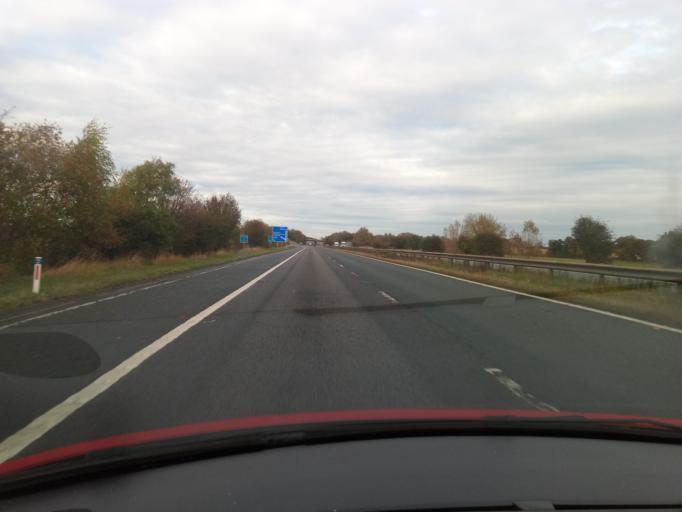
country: GB
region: England
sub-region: Darlington
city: Heighington
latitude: 54.5507
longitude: -1.5995
